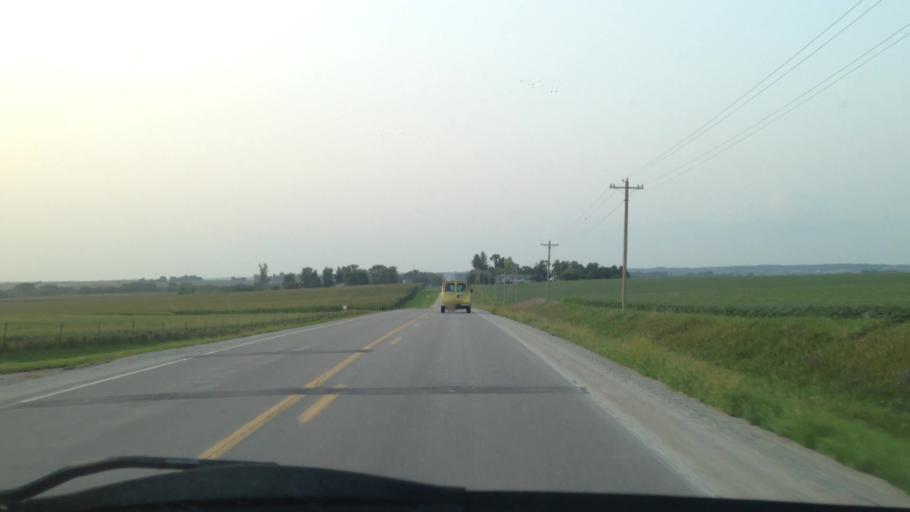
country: US
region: Iowa
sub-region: Benton County
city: Atkins
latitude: 42.0445
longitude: -91.8693
